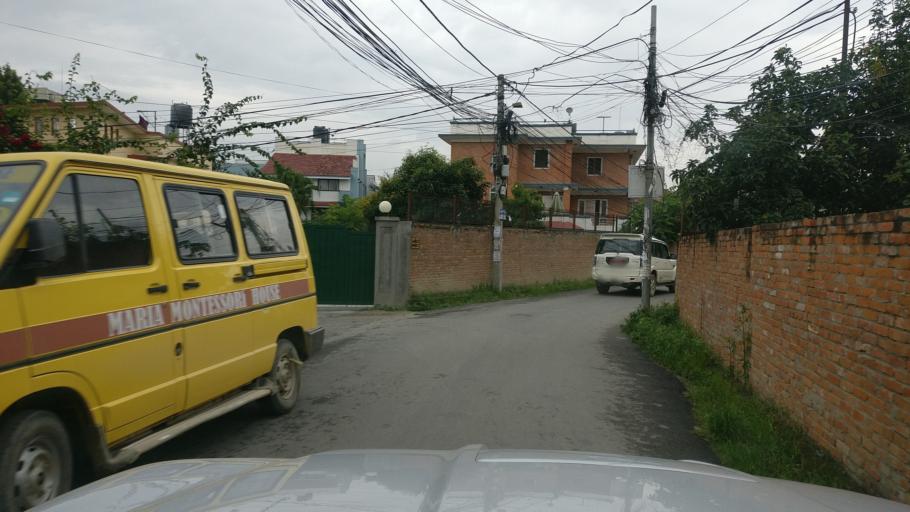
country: NP
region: Central Region
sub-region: Bagmati Zone
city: Patan
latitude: 27.6839
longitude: 85.3083
